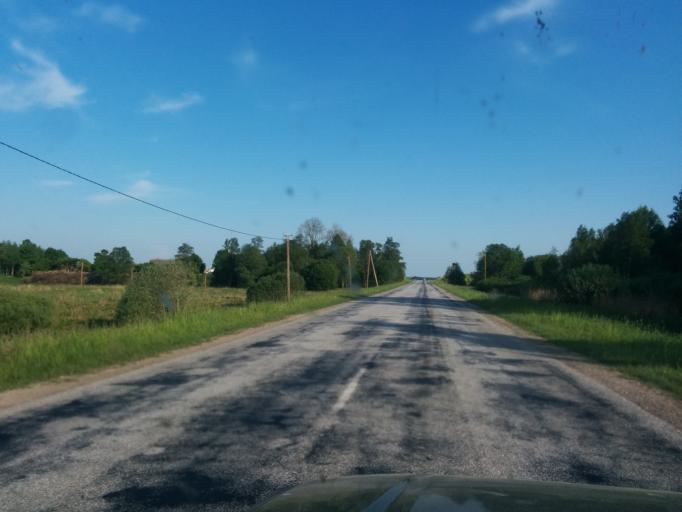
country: LV
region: Talsu Rajons
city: Valdemarpils
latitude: 57.3282
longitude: 22.5202
